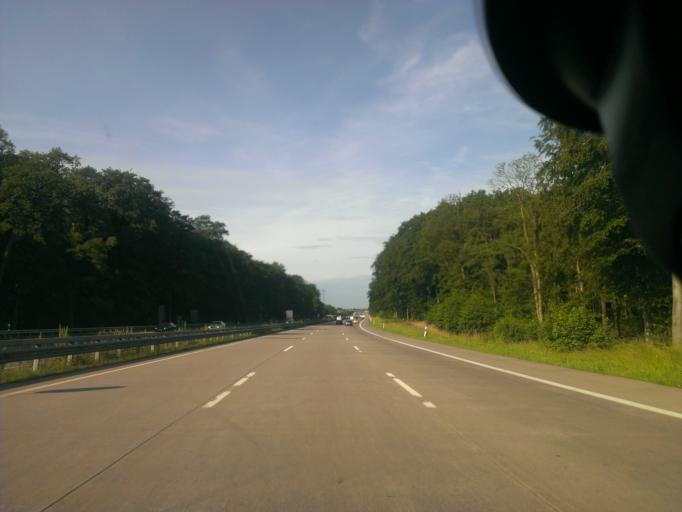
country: DE
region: Schleswig-Holstein
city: Politz
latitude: 53.7769
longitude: 10.4076
